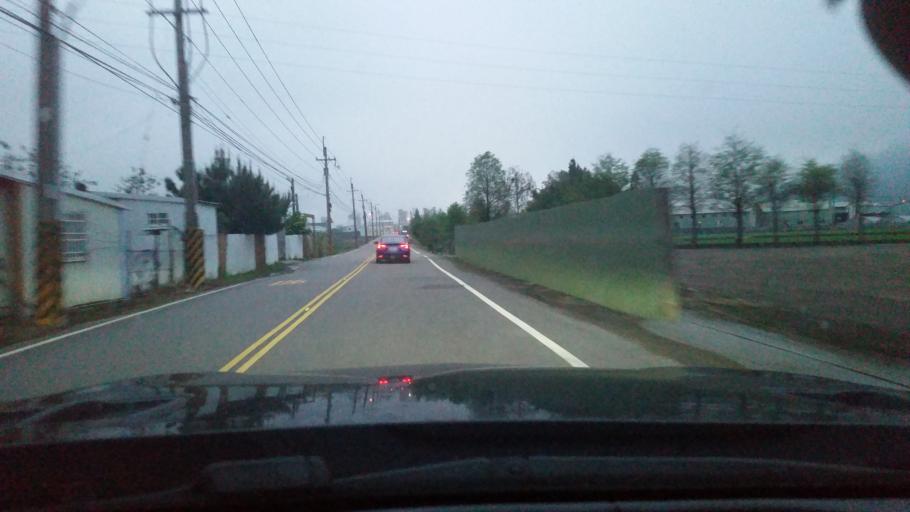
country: TW
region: Taiwan
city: Fengyuan
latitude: 24.3517
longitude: 120.7488
